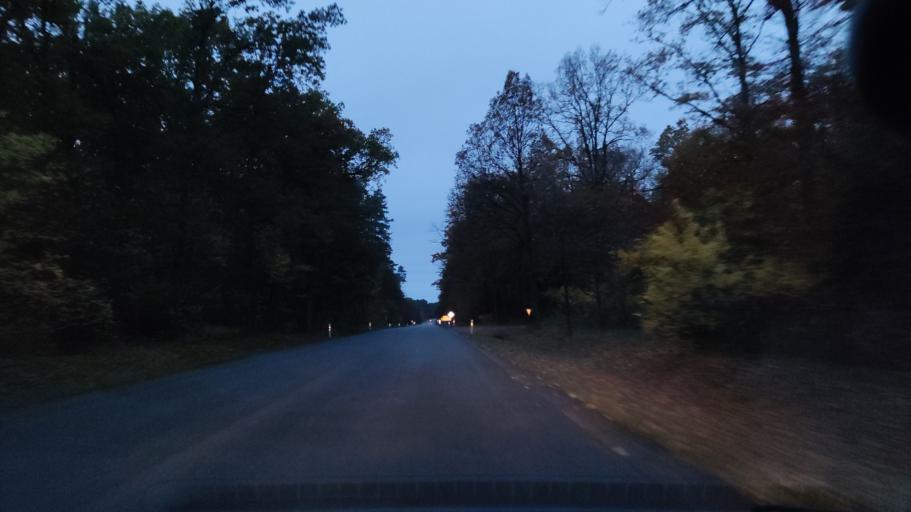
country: DE
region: Lower Saxony
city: Munster
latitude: 53.0103
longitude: 10.1035
